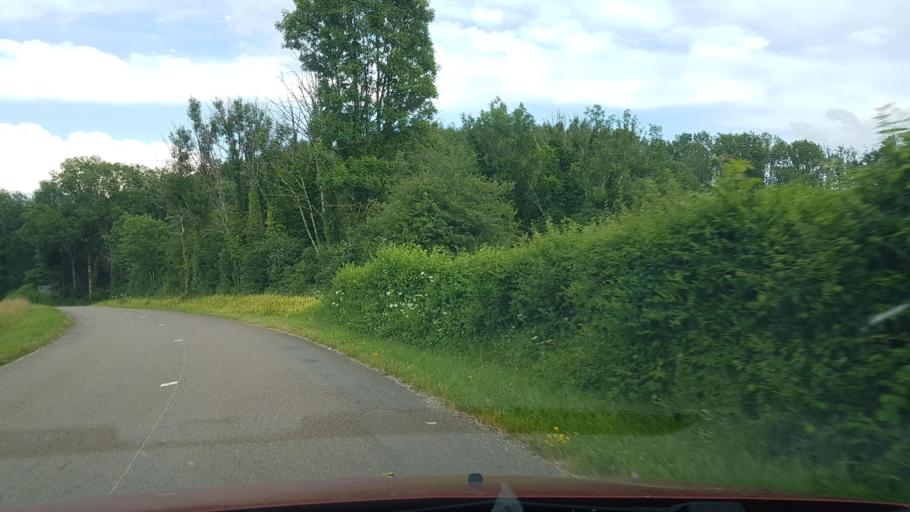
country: FR
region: Franche-Comte
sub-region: Departement du Jura
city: Clairvaux-les-Lacs
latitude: 46.5742
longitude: 5.7414
